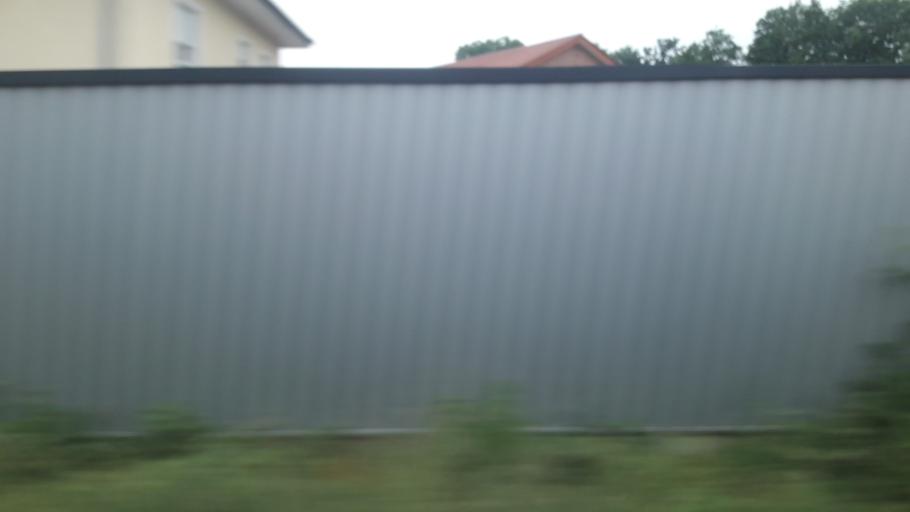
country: DE
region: North Rhine-Westphalia
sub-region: Regierungsbezirk Detmold
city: Hovelhof
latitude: 51.8162
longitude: 8.6695
